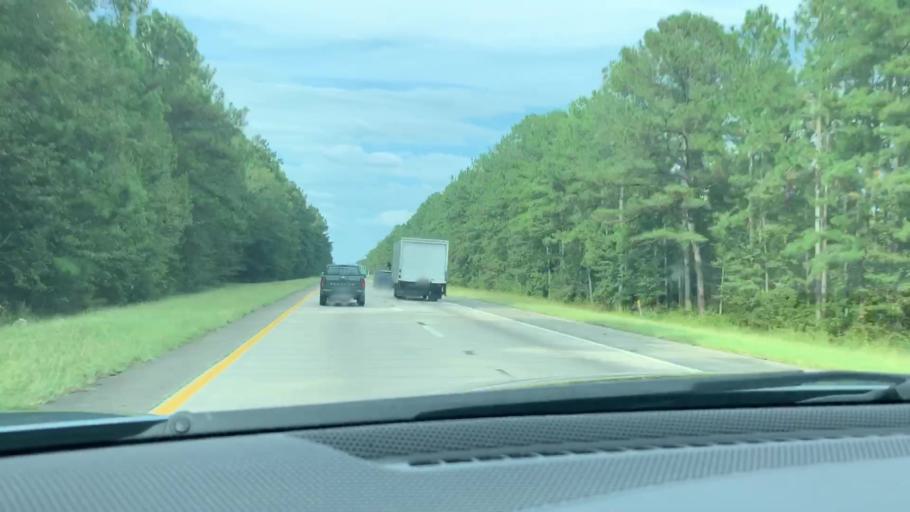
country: US
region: South Carolina
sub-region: Colleton County
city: Walterboro
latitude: 32.9913
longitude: -80.6714
